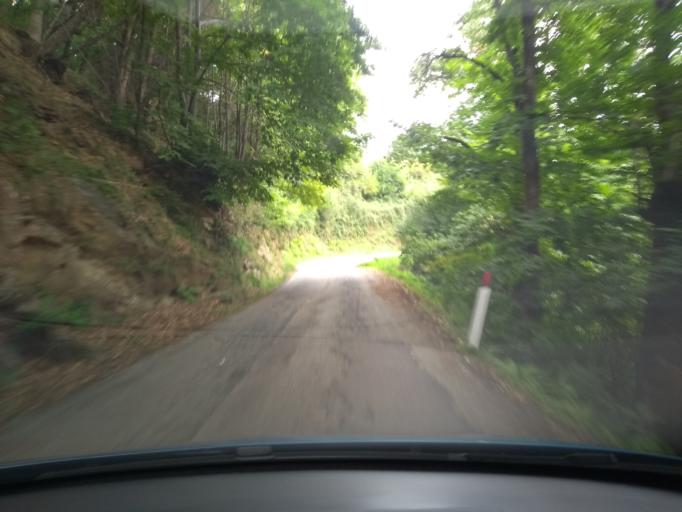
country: IT
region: Piedmont
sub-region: Provincia di Torino
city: Corio
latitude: 45.3334
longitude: 7.5151
